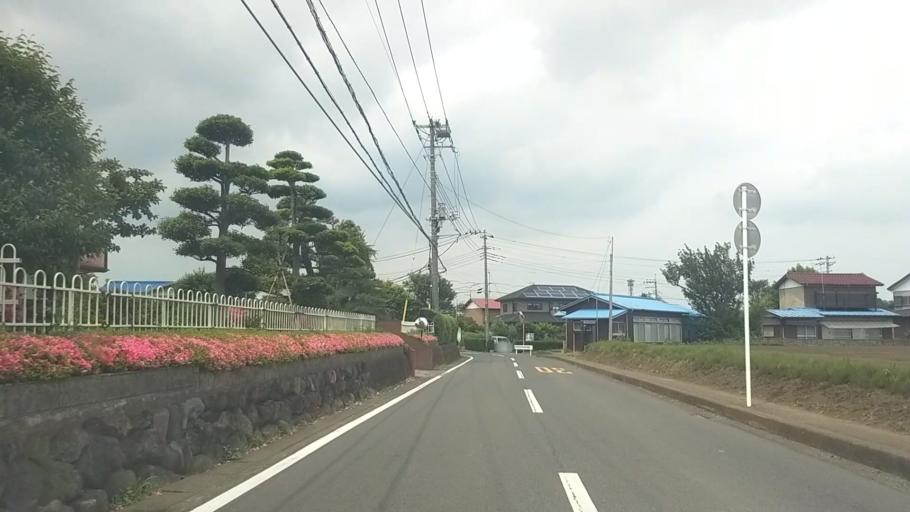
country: JP
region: Kanagawa
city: Chigasaki
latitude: 35.3882
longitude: 139.4140
